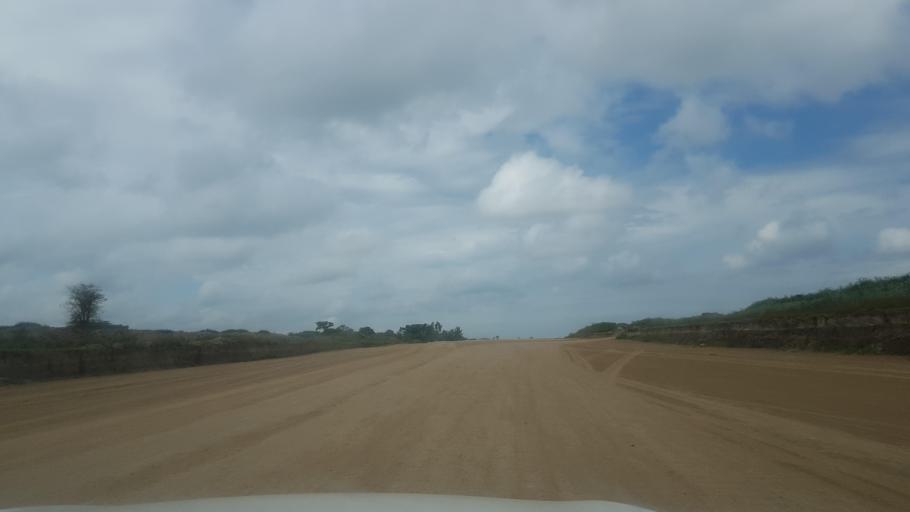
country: ET
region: Oromiya
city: Shashemene
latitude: 7.2478
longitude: 38.5885
